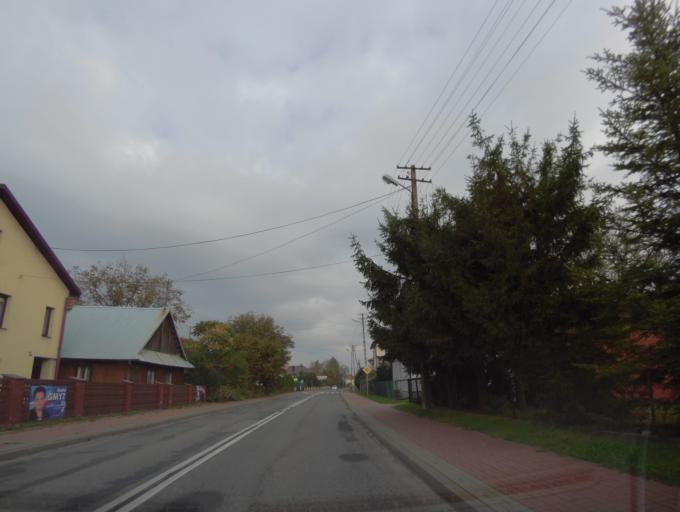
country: PL
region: Lublin Voivodeship
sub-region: Powiat bilgorajski
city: Frampol
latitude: 50.6684
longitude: 22.6708
